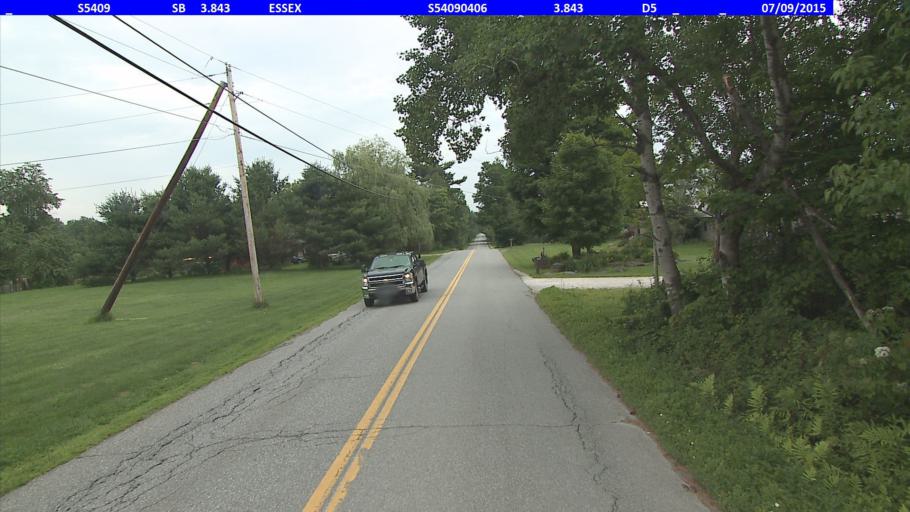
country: US
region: Vermont
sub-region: Chittenden County
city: Essex Junction
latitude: 44.5626
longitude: -73.0632
